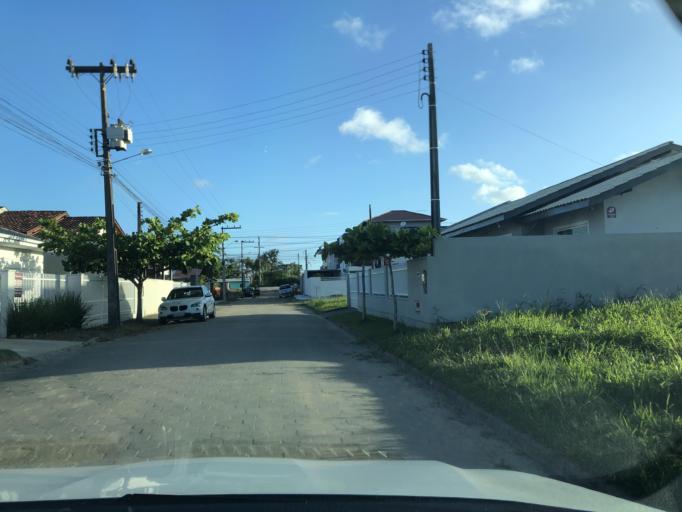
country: BR
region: Santa Catarina
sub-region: Sao Francisco Do Sul
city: Sao Francisco do Sul
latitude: -26.2226
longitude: -48.5267
